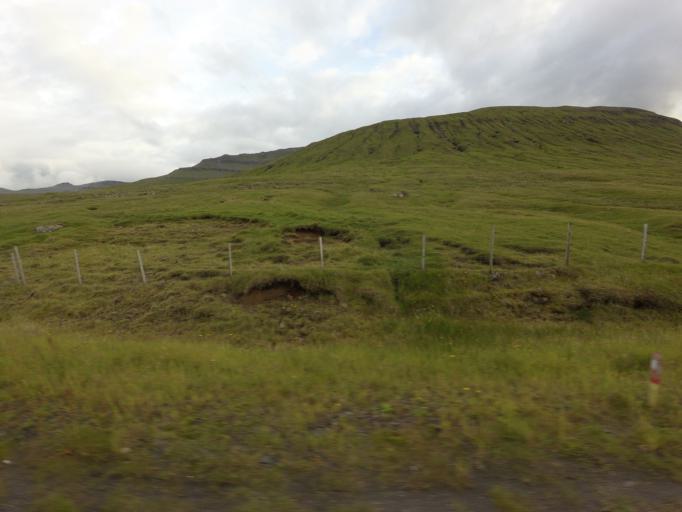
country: FO
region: Streymoy
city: Kollafjordhur
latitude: 62.1789
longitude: -6.9851
